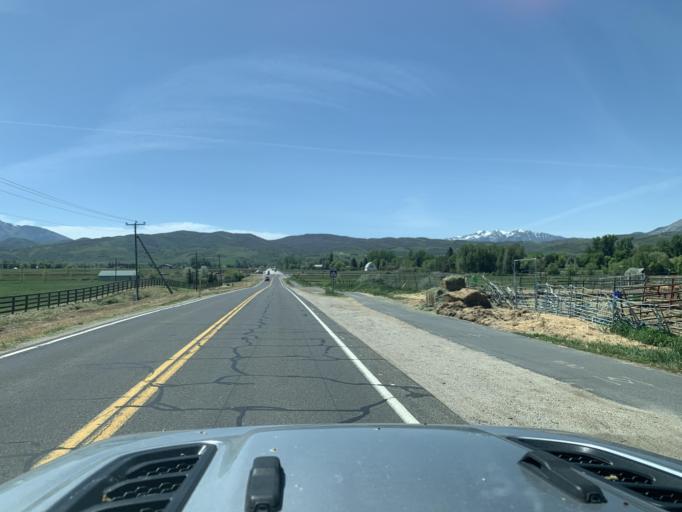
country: US
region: Utah
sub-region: Weber County
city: Wolf Creek
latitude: 41.2662
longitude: -111.7617
